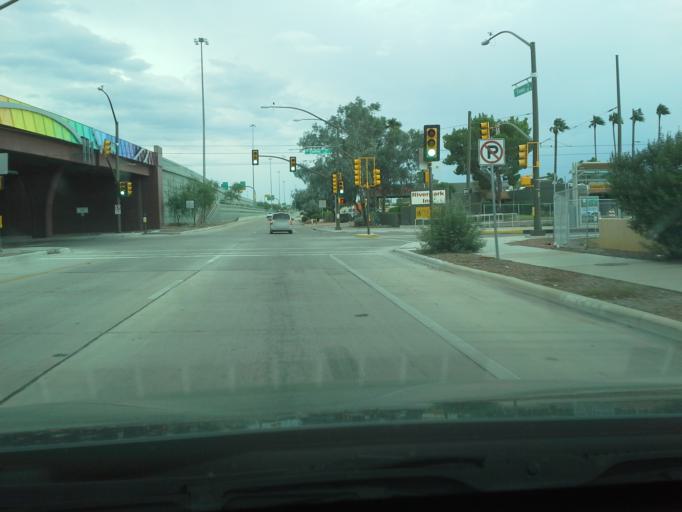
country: US
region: Arizona
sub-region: Pima County
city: South Tucson
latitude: 32.2177
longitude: -110.9802
